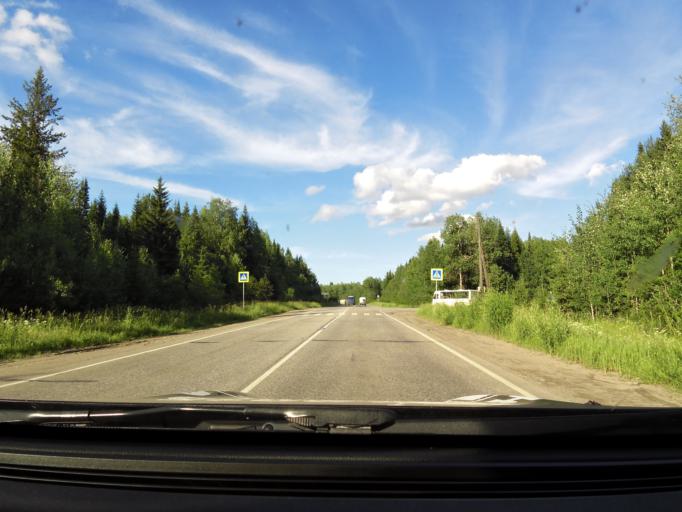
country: RU
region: Kirov
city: Omutninsk
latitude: 58.6996
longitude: 52.2355
